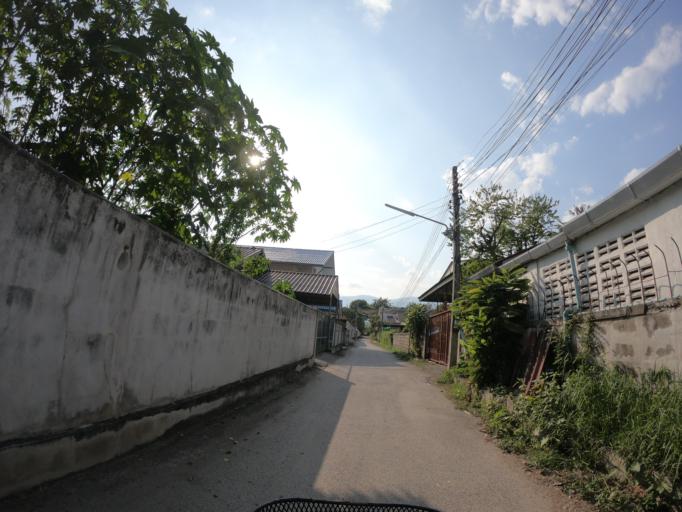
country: TH
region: Chiang Mai
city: Chiang Mai
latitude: 18.8346
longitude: 98.9853
